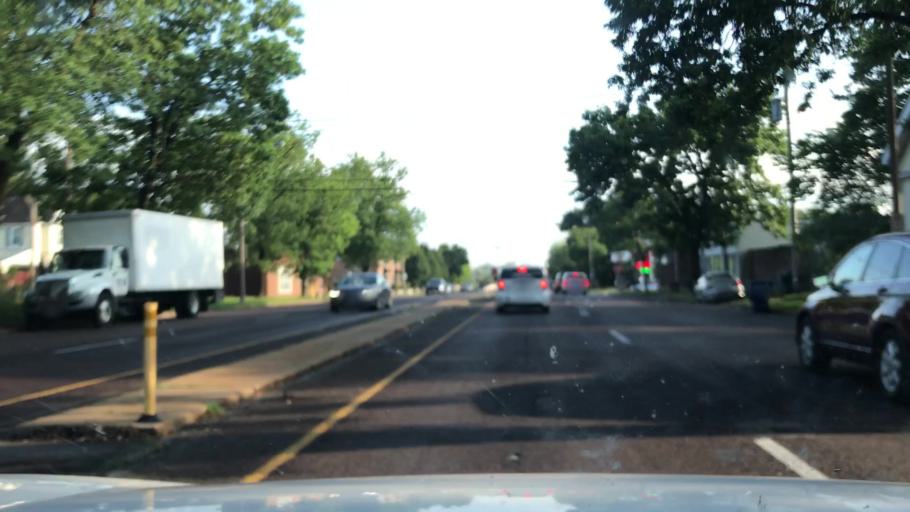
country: US
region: Missouri
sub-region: Saint Louis County
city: Maplewood
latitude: 38.6027
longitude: -90.3078
